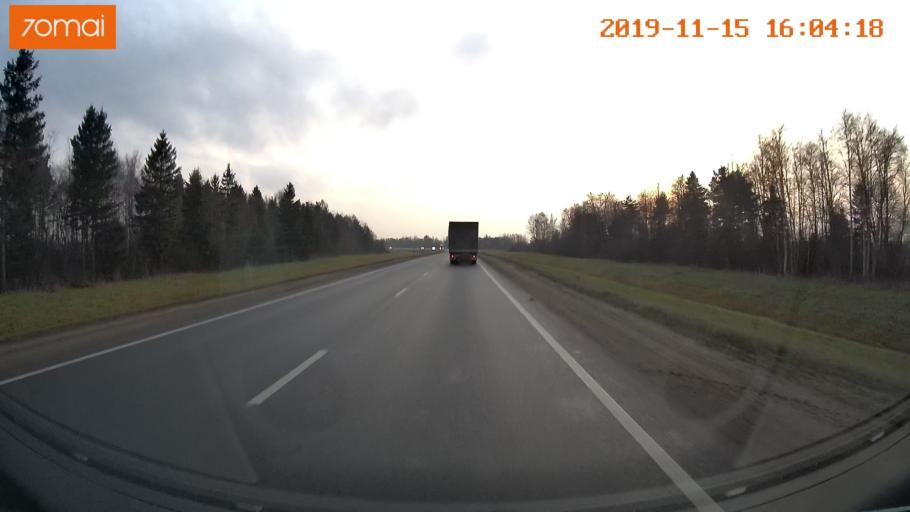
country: RU
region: Jaroslavl
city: Yaroslavl
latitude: 57.7494
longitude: 39.9034
